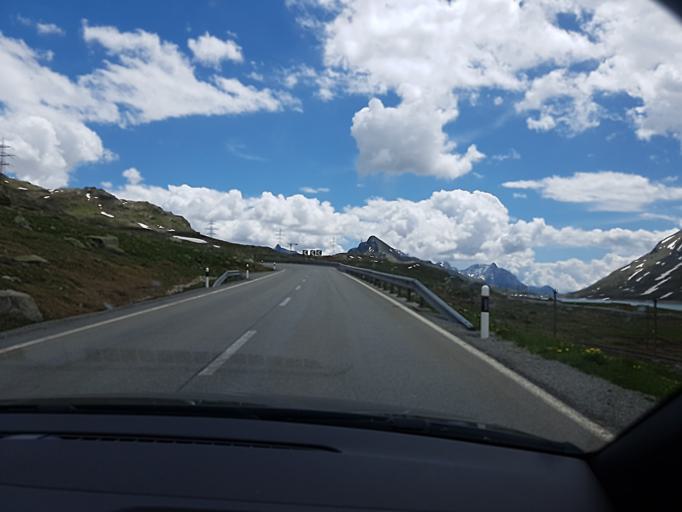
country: CH
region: Grisons
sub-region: Bernina District
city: Poschiavo
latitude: 46.4183
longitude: 10.0087
